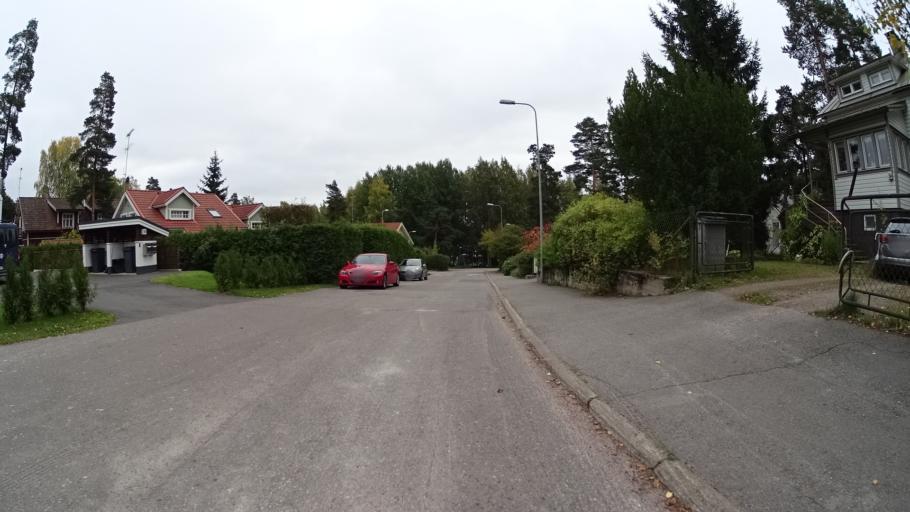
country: FI
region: Uusimaa
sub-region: Helsinki
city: Vantaa
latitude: 60.2145
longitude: 25.0465
